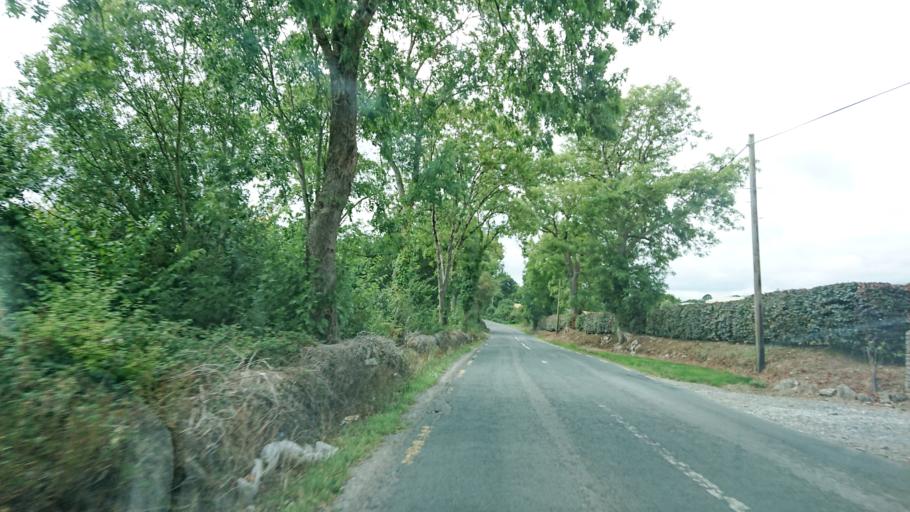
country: IE
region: Munster
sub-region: County Cork
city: Mallow
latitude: 52.1522
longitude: -8.5324
